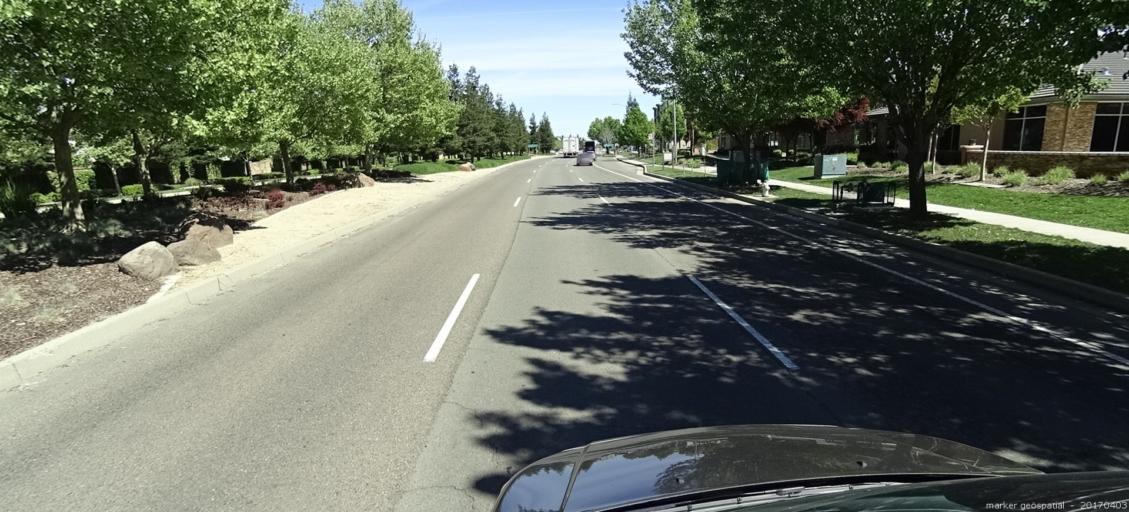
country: US
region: California
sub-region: Sacramento County
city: Rio Linda
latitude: 38.6560
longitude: -121.5060
